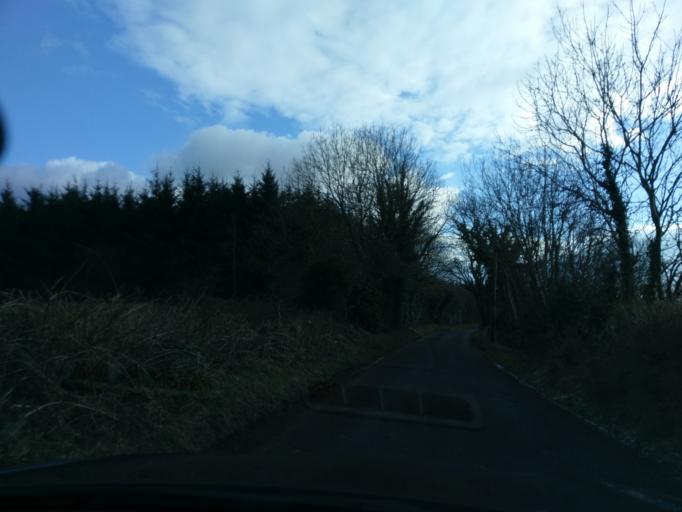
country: IE
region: Connaught
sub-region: County Galway
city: Athenry
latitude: 53.3829
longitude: -8.6241
